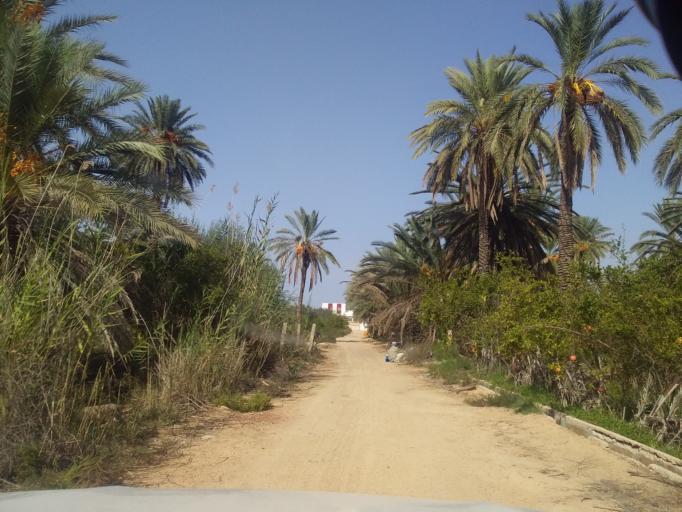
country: TN
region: Qabis
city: Gabes
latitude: 33.6288
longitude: 10.2864
